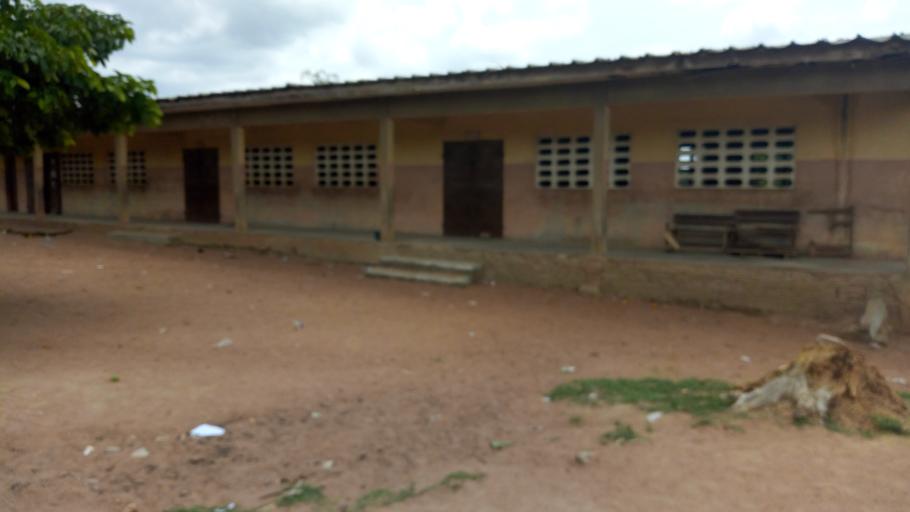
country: CI
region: Vallee du Bandama
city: Bouake
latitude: 7.7052
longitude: -4.9881
